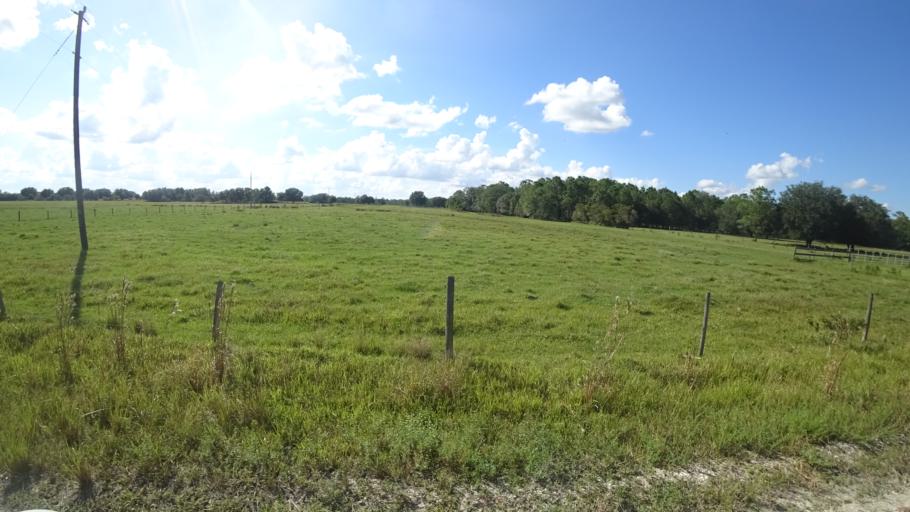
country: US
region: Florida
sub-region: Hardee County
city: Wauchula
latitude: 27.4625
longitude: -82.0555
